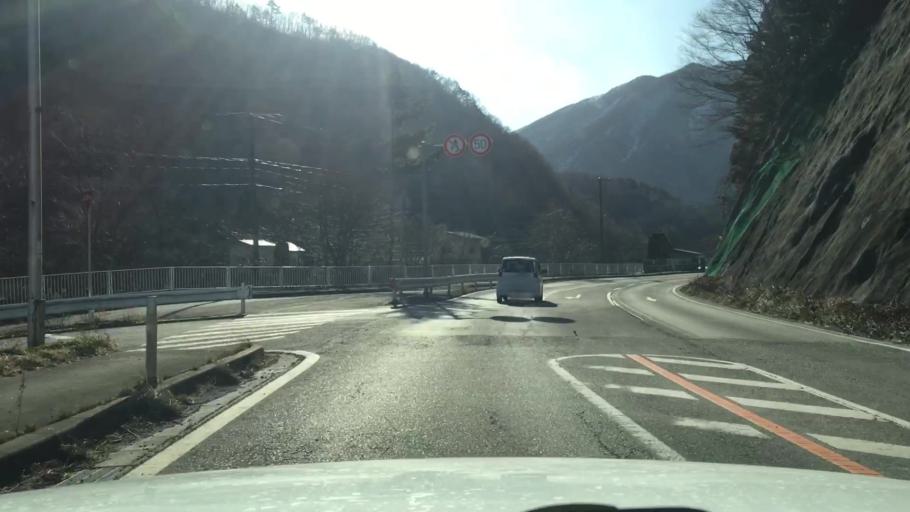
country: JP
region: Iwate
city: Miyako
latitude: 39.5935
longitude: 141.6750
